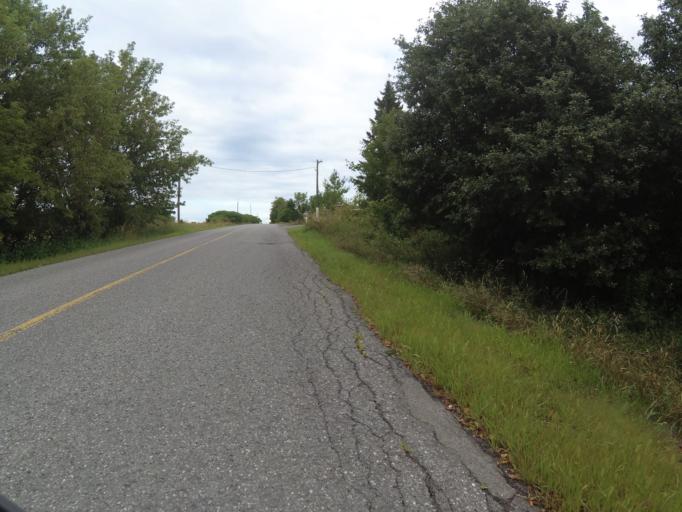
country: CA
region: Ontario
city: Clarence-Rockland
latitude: 45.4298
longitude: -75.2996
